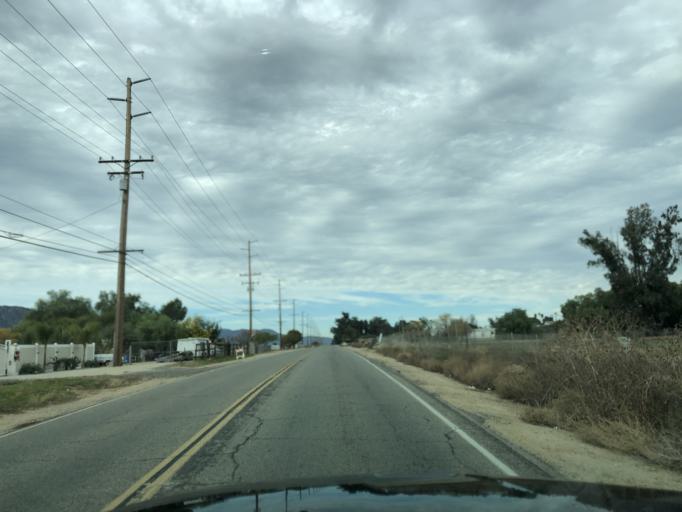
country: US
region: California
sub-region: Riverside County
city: Wildomar
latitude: 33.6087
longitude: -117.2808
